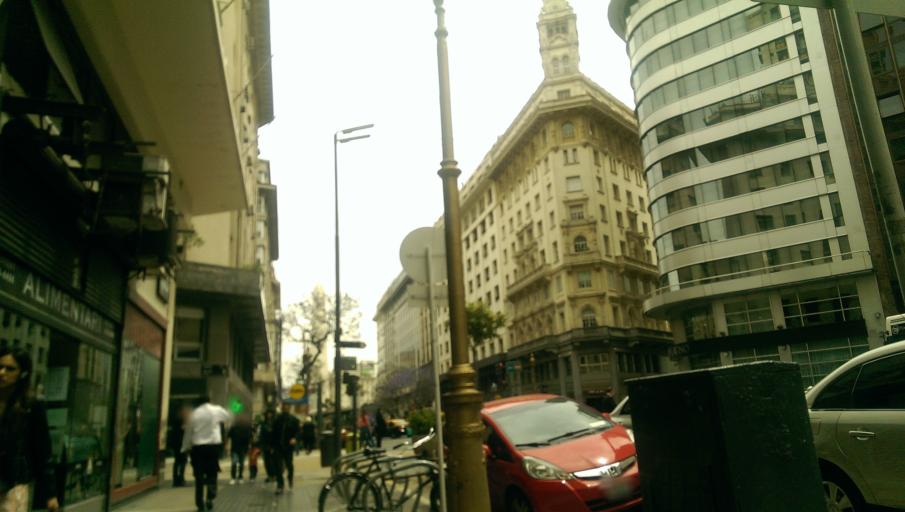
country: AR
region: Buenos Aires F.D.
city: Buenos Aires
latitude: -34.6049
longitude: -58.3790
